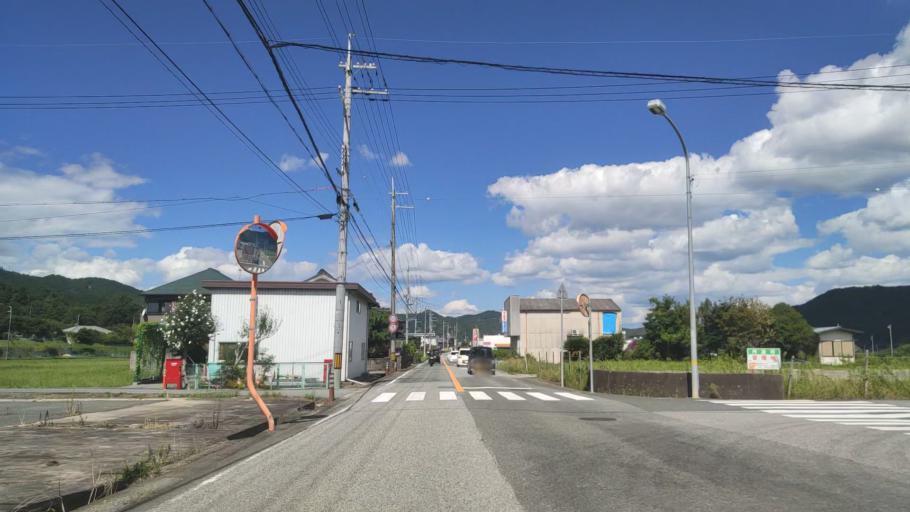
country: JP
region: Kyoto
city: Fukuchiyama
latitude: 35.2200
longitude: 135.1305
